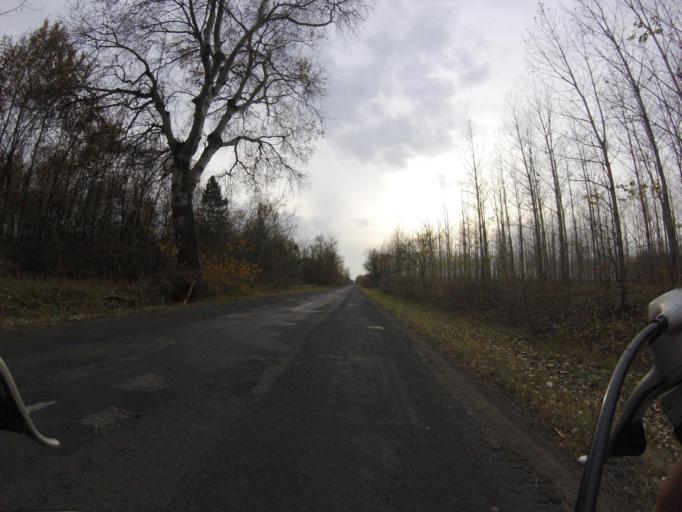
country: HU
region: Pest
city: Csemo
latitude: 47.1039
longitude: 19.6206
